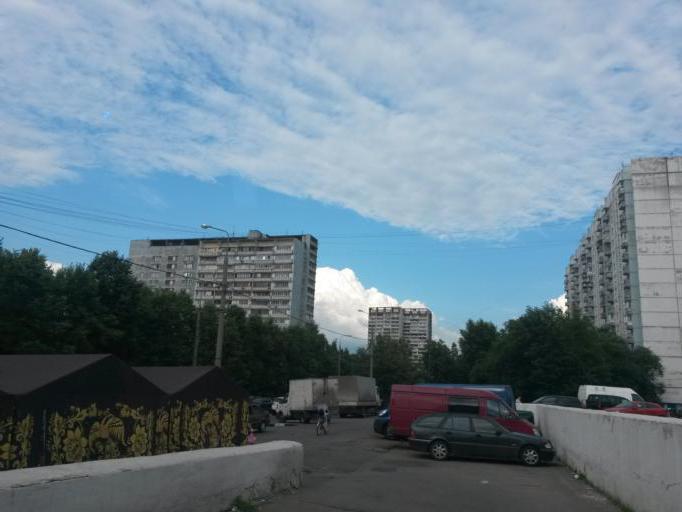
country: RU
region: Moscow
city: Orekhovo-Borisovo
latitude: 55.6216
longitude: 37.7383
